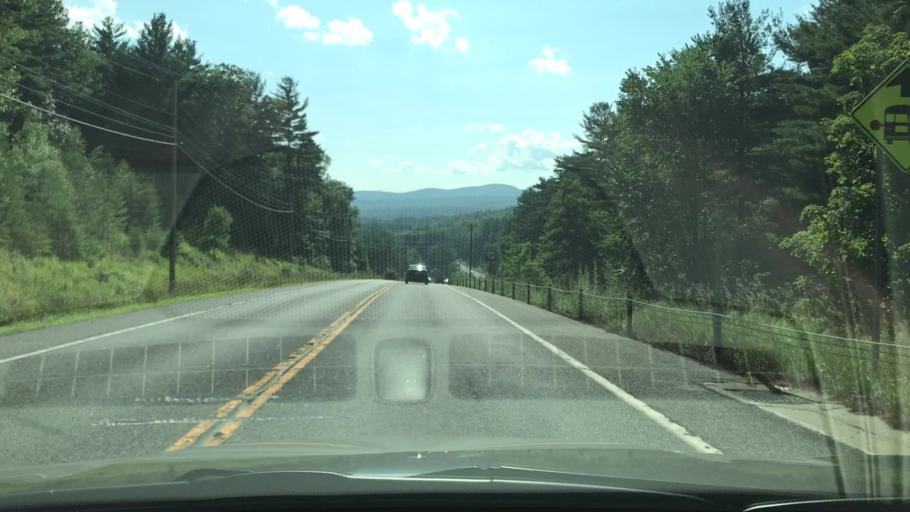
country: US
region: New York
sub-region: Warren County
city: Glens Falls North
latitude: 43.3757
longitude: -73.6677
